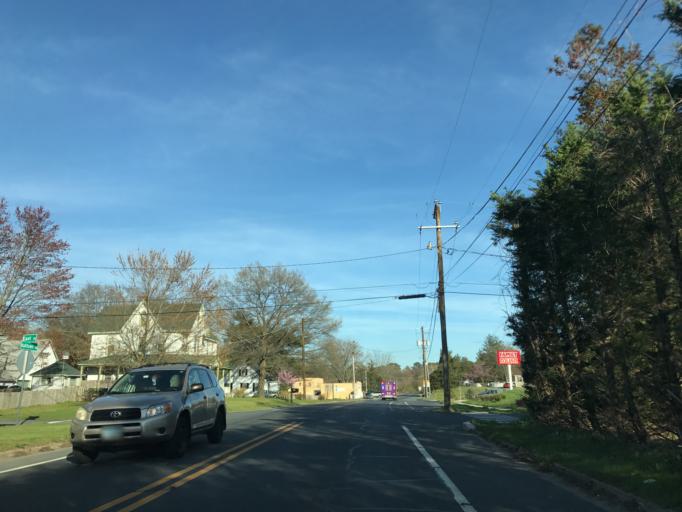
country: US
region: Maryland
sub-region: Caroline County
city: Greensboro
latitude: 39.1124
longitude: -75.7450
